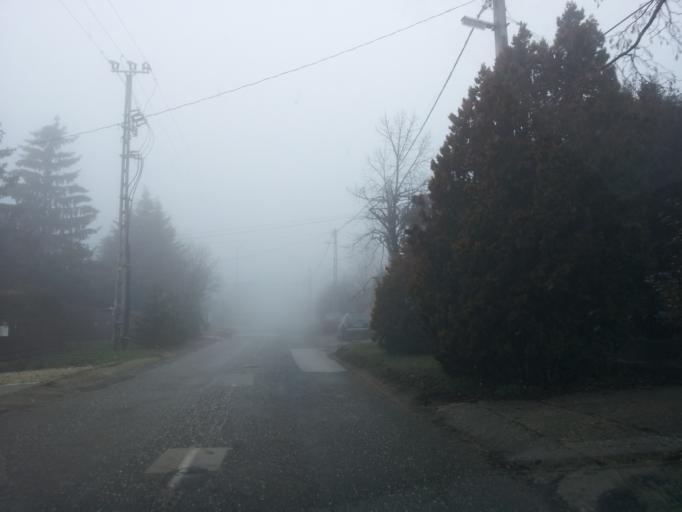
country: HU
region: Pest
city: Toeroekbalint
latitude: 47.4230
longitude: 18.8805
